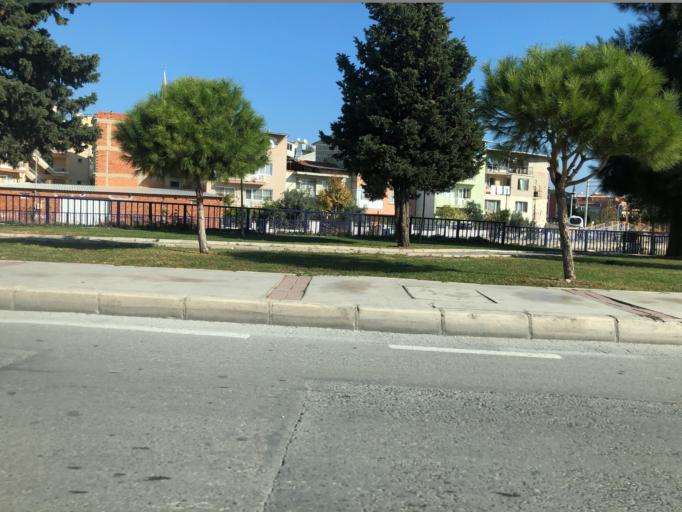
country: TR
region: Izmir
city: Izmir
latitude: 38.4605
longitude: 27.1733
